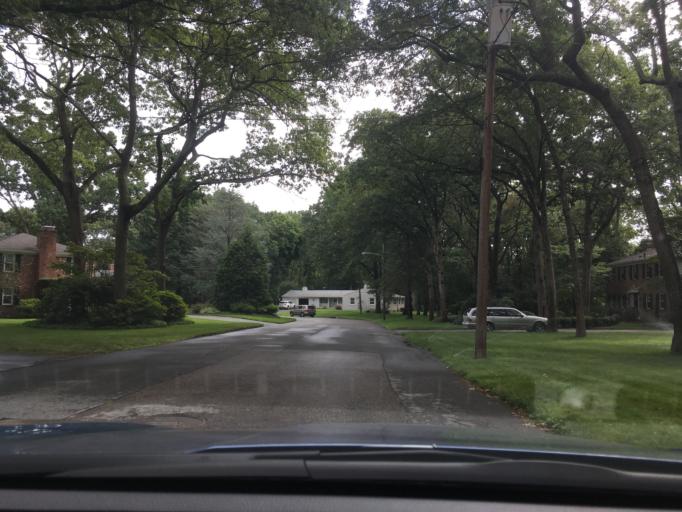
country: US
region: Rhode Island
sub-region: Kent County
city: East Greenwich
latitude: 41.6423
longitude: -71.4788
